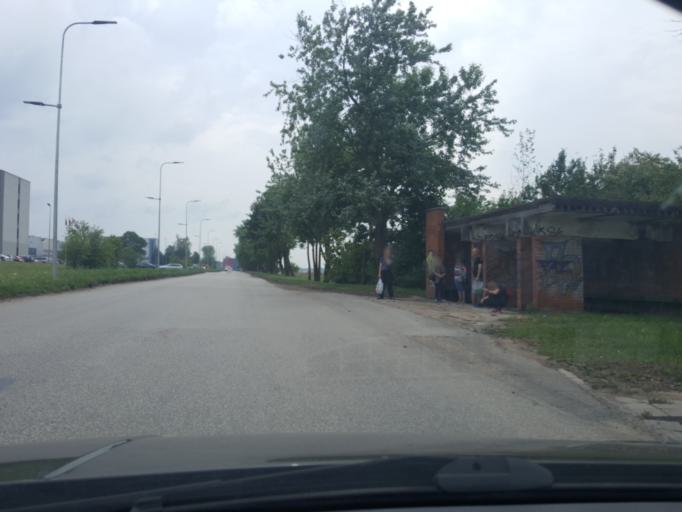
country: LT
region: Alytaus apskritis
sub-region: Alytus
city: Alytus
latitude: 54.4350
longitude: 24.0046
